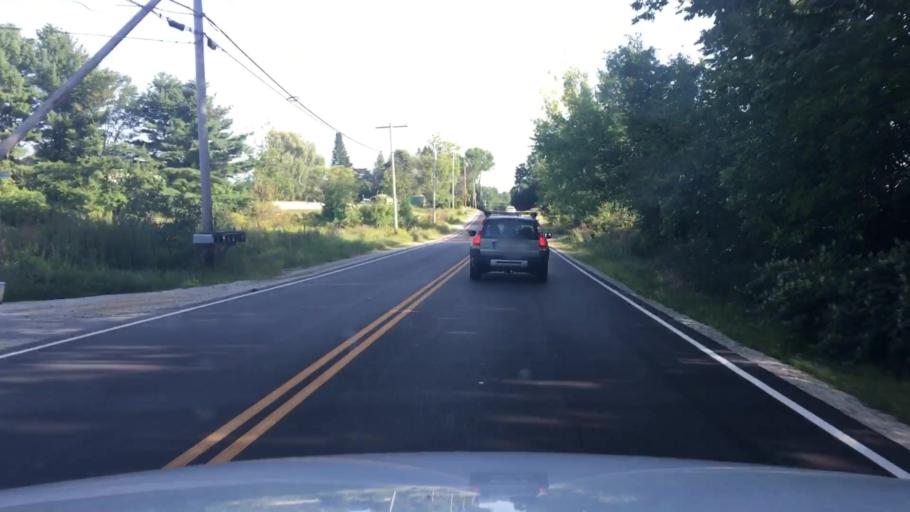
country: US
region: Maine
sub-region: Cumberland County
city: Cumberland Center
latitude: 43.8042
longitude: -70.3095
